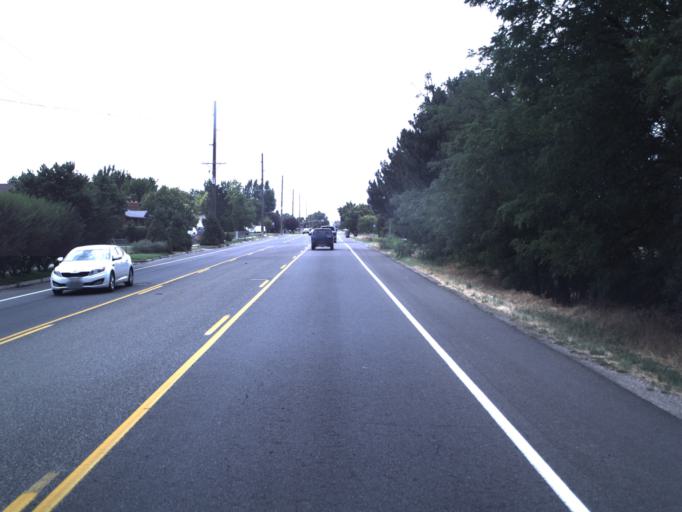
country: US
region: Utah
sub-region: Davis County
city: Clinton
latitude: 41.1670
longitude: -112.0645
